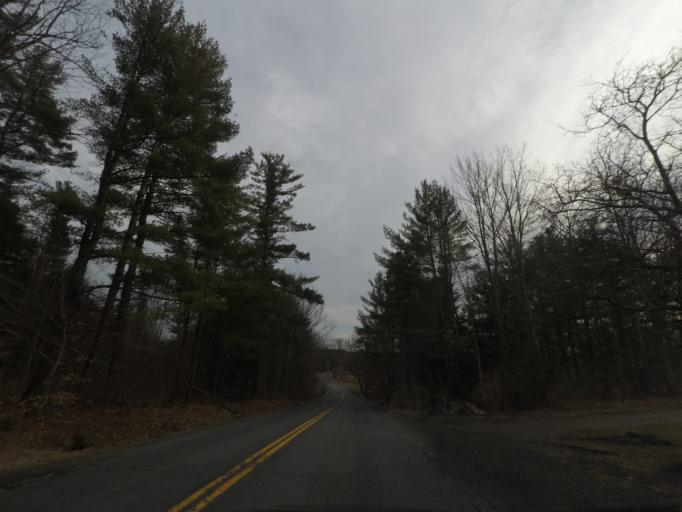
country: US
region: New York
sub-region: Rensselaer County
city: Hoosick Falls
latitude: 42.8510
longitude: -73.4555
